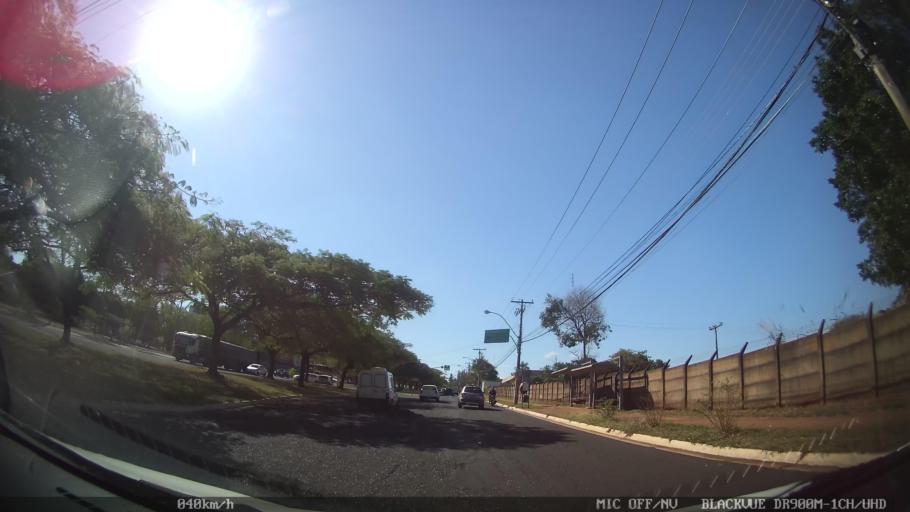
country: BR
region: Sao Paulo
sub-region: Ribeirao Preto
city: Ribeirao Preto
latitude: -21.2051
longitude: -47.7689
